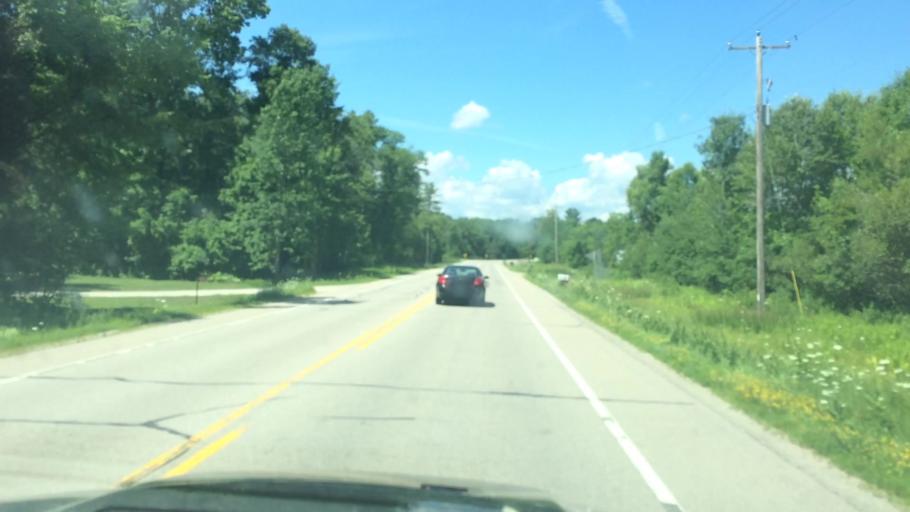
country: US
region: Wisconsin
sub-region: Marinette County
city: Peshtigo
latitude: 45.1004
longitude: -87.7387
